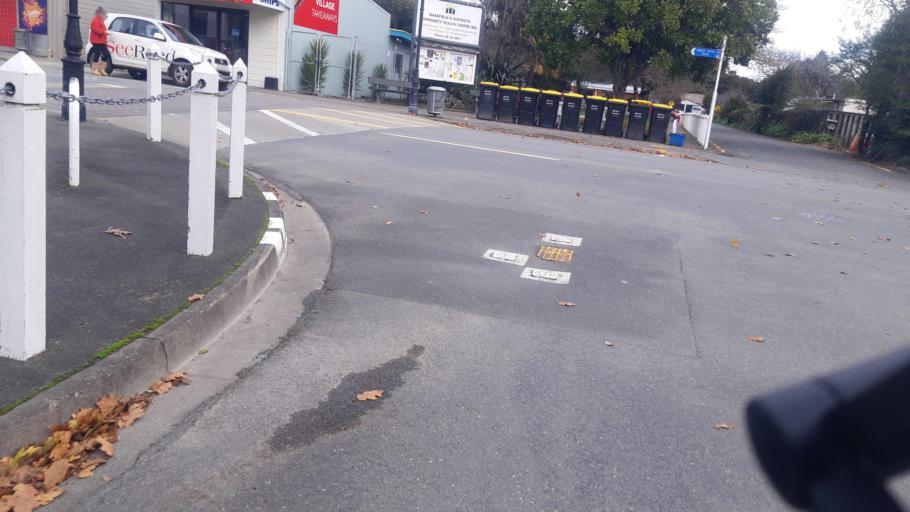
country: NZ
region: Tasman
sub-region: Tasman District
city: Wakefield
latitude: -41.4058
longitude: 173.0429
